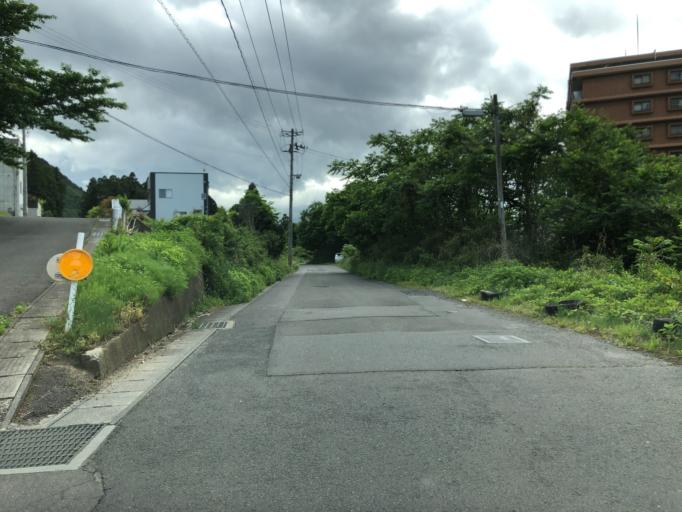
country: JP
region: Fukushima
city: Fukushima-shi
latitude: 37.7794
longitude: 140.4716
